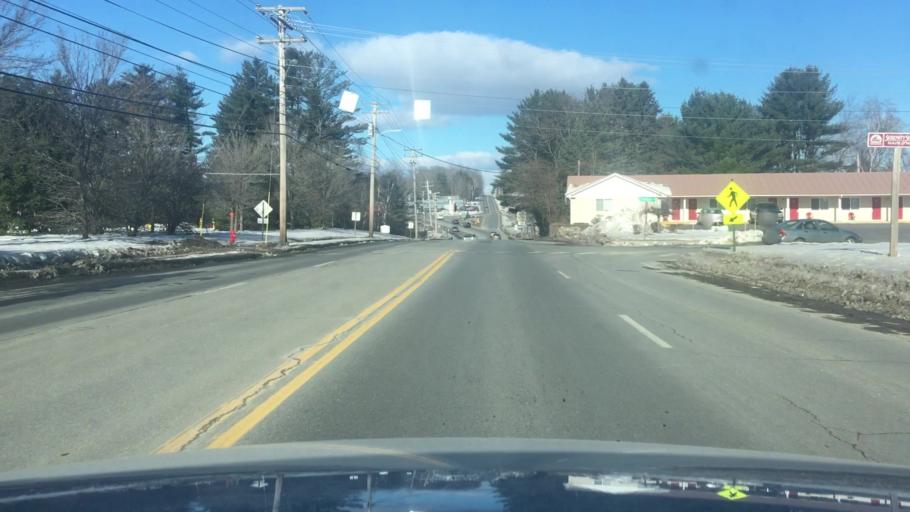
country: US
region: Maine
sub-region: Somerset County
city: Skowhegan
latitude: 44.7805
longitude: -69.7264
